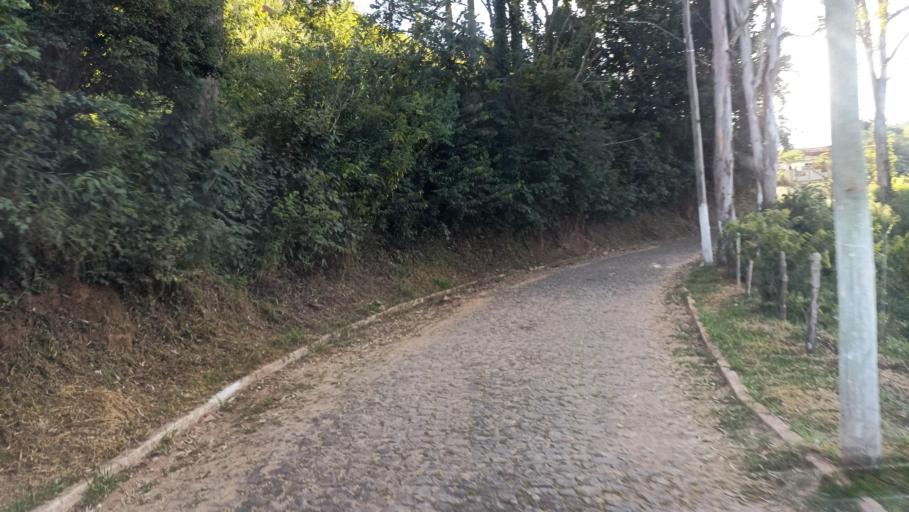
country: BR
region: Minas Gerais
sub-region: Ouro Preto
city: Ouro Preto
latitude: -20.3132
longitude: -43.5836
